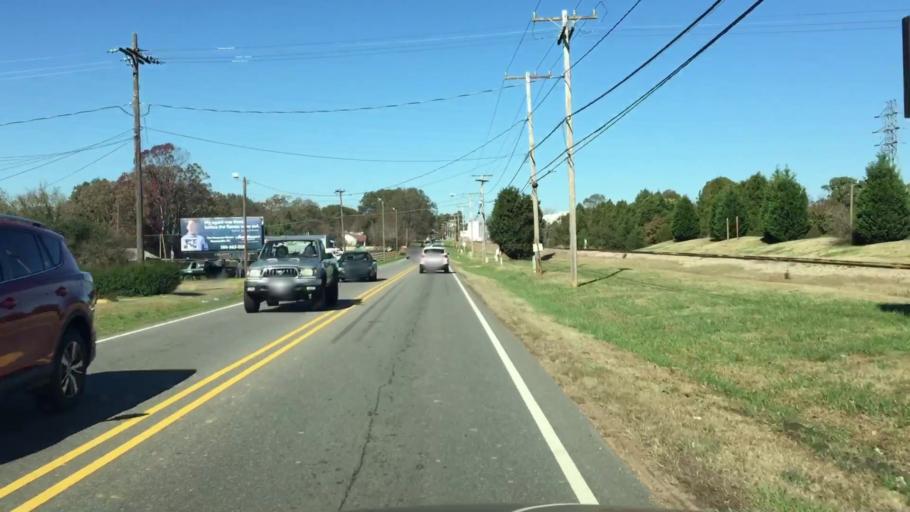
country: US
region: North Carolina
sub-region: Iredell County
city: Mooresville
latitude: 35.6075
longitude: -80.8160
